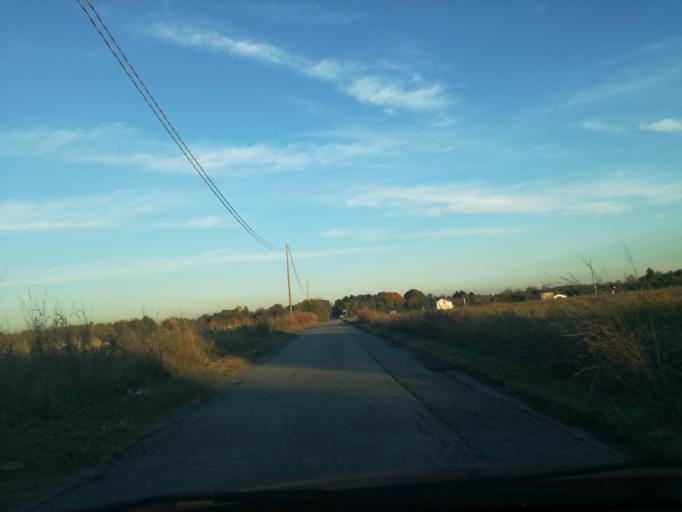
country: IT
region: Lombardy
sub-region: Provincia di Monza e Brianza
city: Burago di Molgora
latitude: 45.6061
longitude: 9.3840
